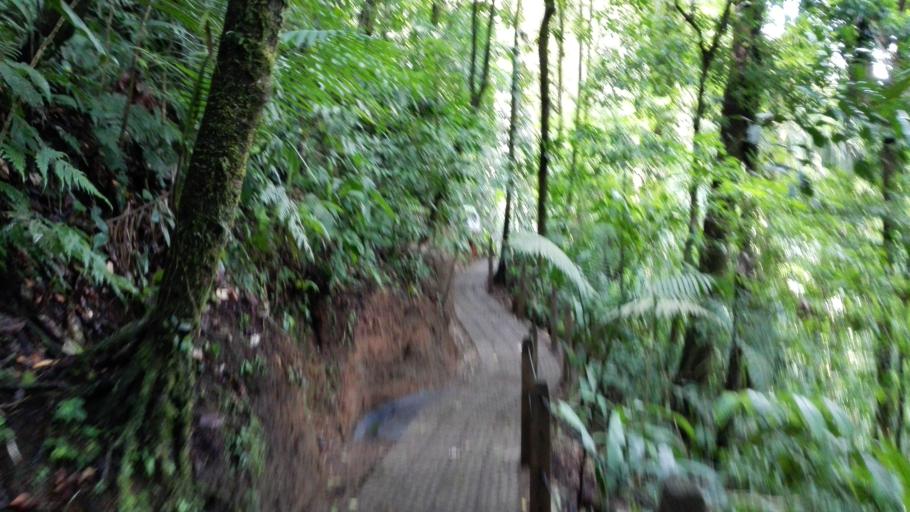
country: CR
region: Alajuela
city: La Fortuna
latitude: 10.4950
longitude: -84.7523
